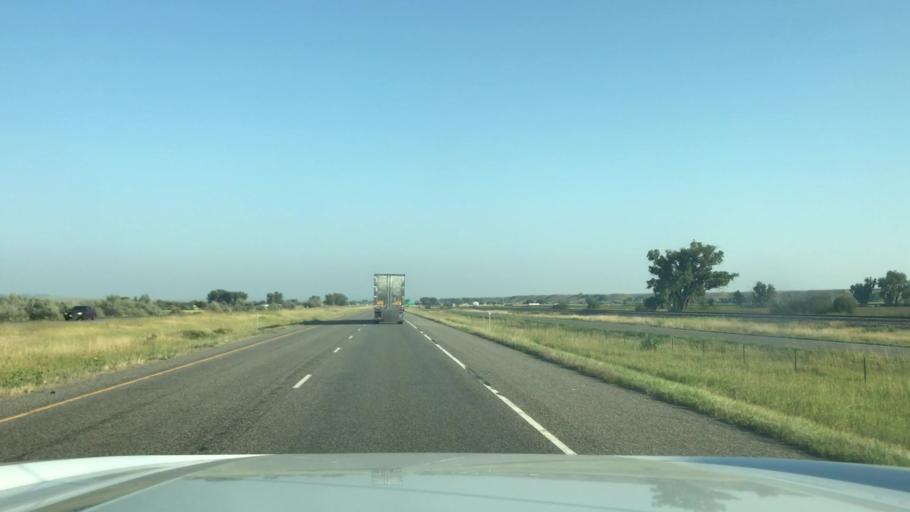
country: US
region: Montana
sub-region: Big Horn County
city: Hardin
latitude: 45.6993
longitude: -107.5229
